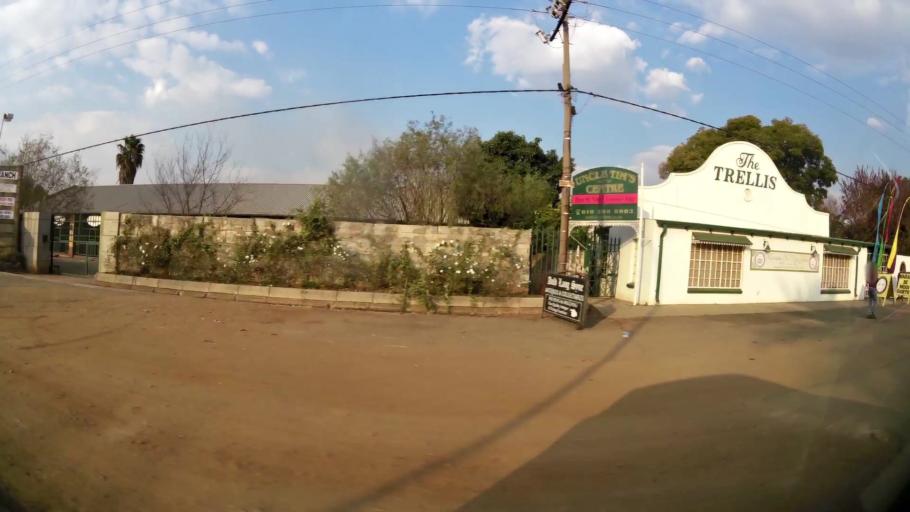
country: ZA
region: Gauteng
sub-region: Ekurhuleni Metropolitan Municipality
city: Benoni
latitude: -26.1225
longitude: 28.2938
